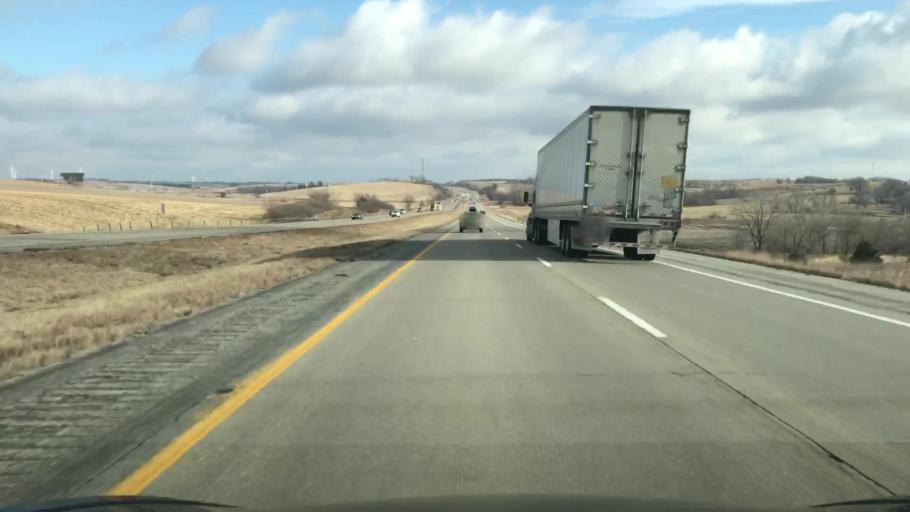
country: US
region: Iowa
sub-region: Cass County
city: Atlantic
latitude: 41.4967
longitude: -94.8033
